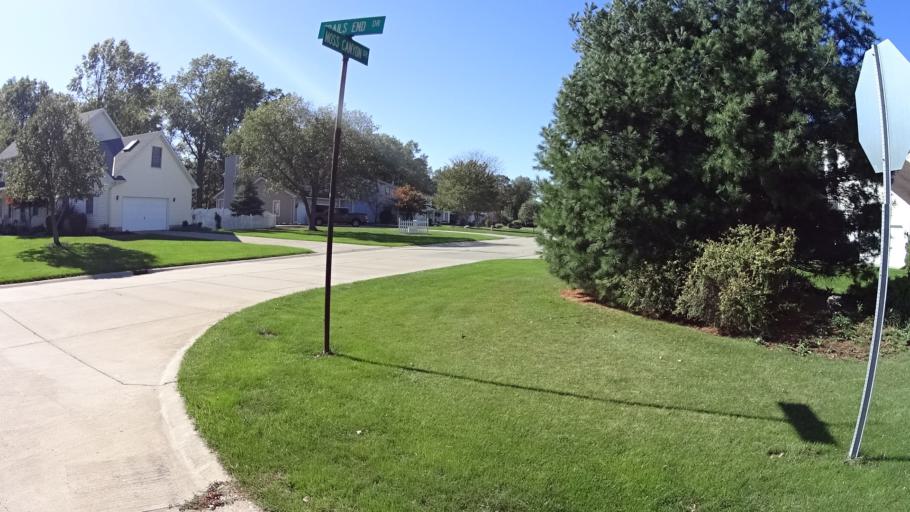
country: US
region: Ohio
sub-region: Lorain County
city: Amherst
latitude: 41.3985
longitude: -82.1922
